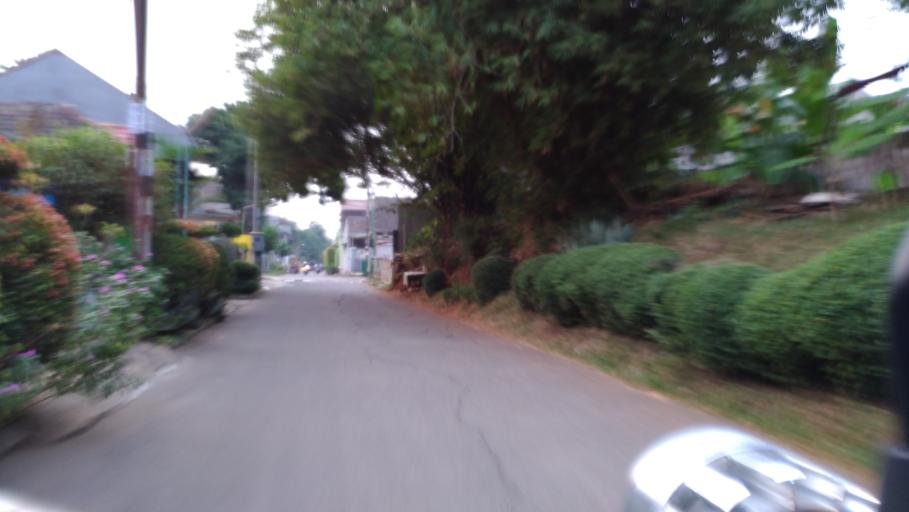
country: ID
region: West Java
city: Depok
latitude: -6.3632
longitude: 106.8659
